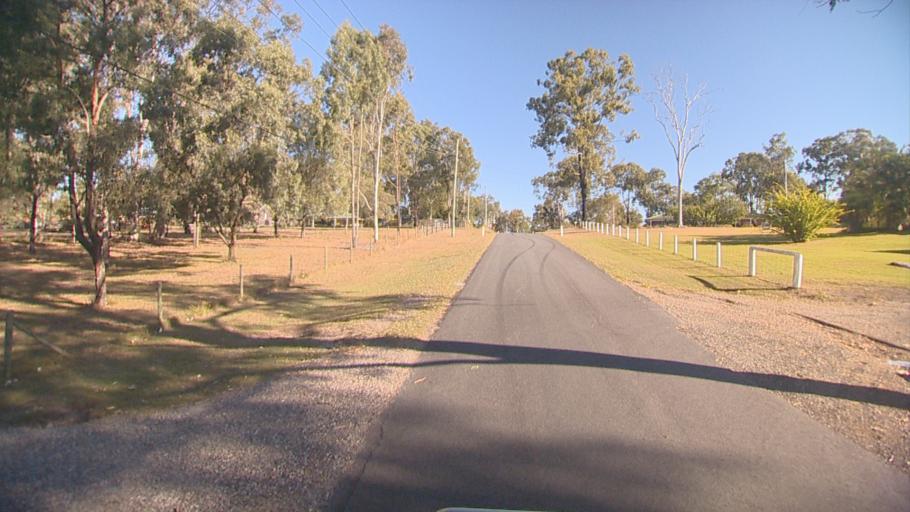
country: AU
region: Queensland
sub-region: Logan
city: Logan Reserve
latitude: -27.7437
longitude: 153.1083
